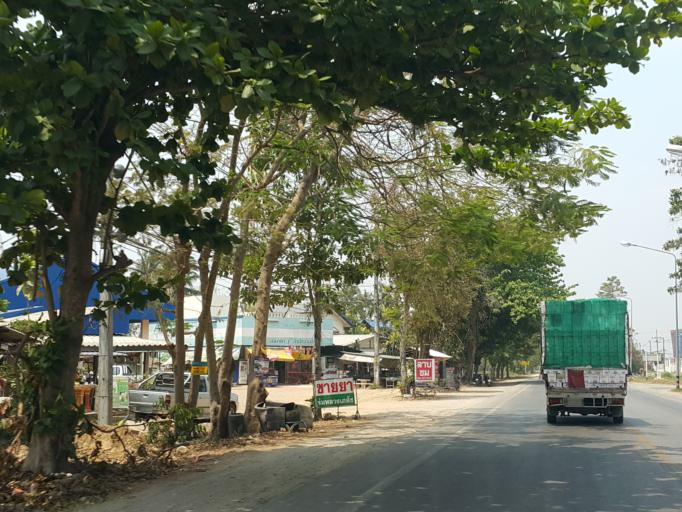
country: TH
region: Chiang Mai
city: Mae Taeng
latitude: 19.0413
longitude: 98.9685
